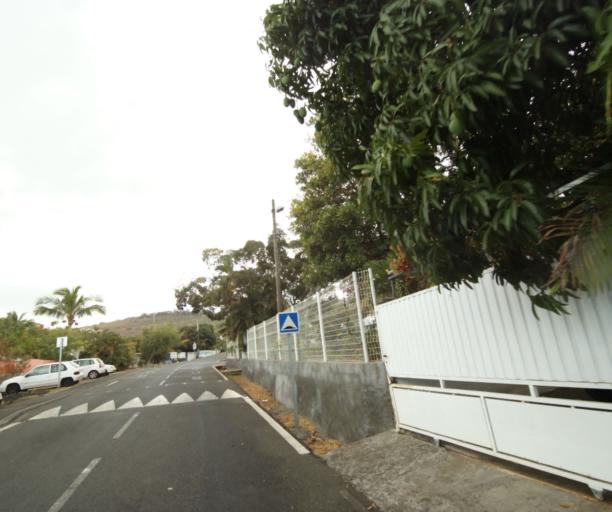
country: RE
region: Reunion
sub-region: Reunion
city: Saint-Paul
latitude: -21.0536
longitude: 55.2334
